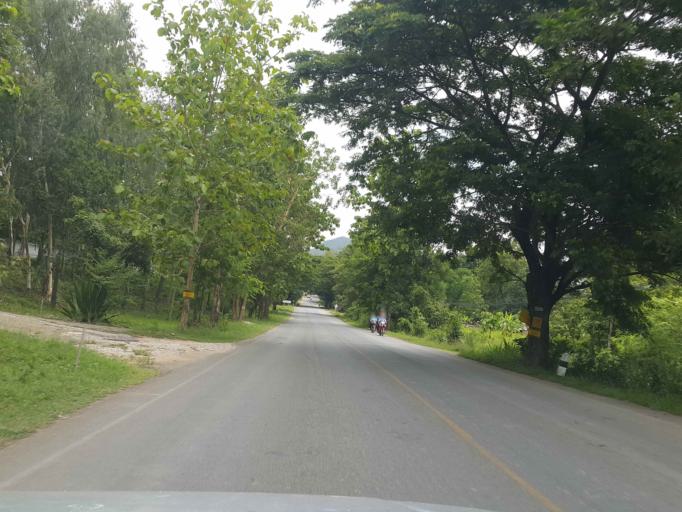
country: TH
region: Lampang
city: Thoen
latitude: 17.5932
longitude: 99.3316
